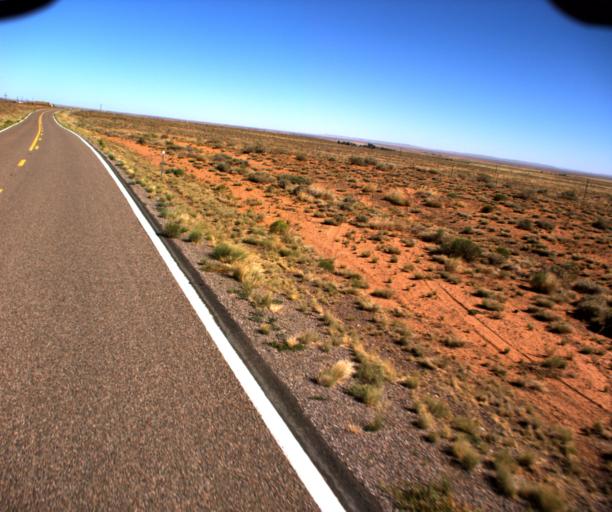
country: US
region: Arizona
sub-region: Coconino County
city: LeChee
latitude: 35.1110
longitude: -110.8678
